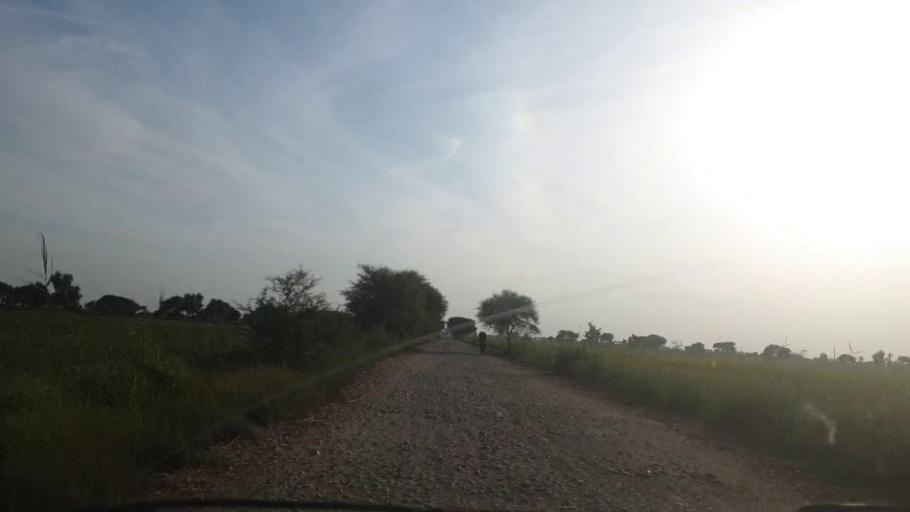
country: PK
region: Sindh
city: Tando Muhammad Khan
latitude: 25.2098
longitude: 68.5053
